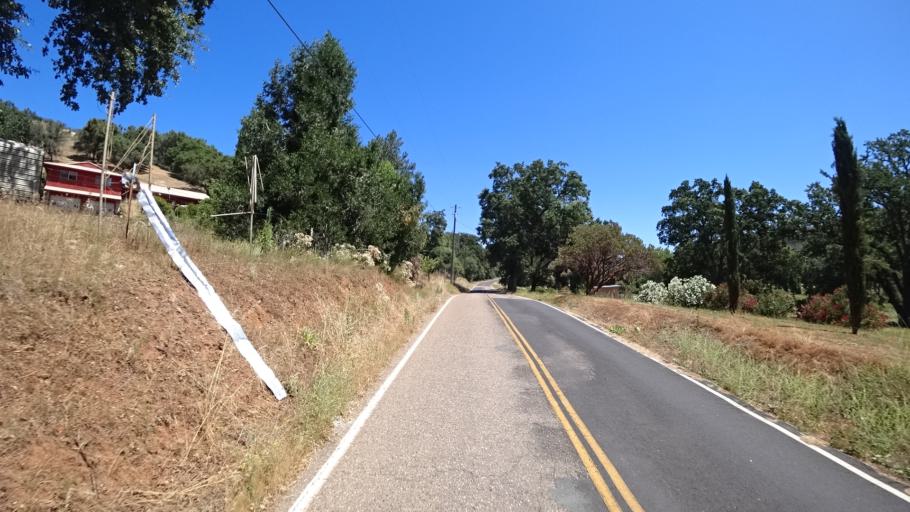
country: US
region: California
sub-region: Calaveras County
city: Mountain Ranch
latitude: 38.2020
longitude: -120.5619
